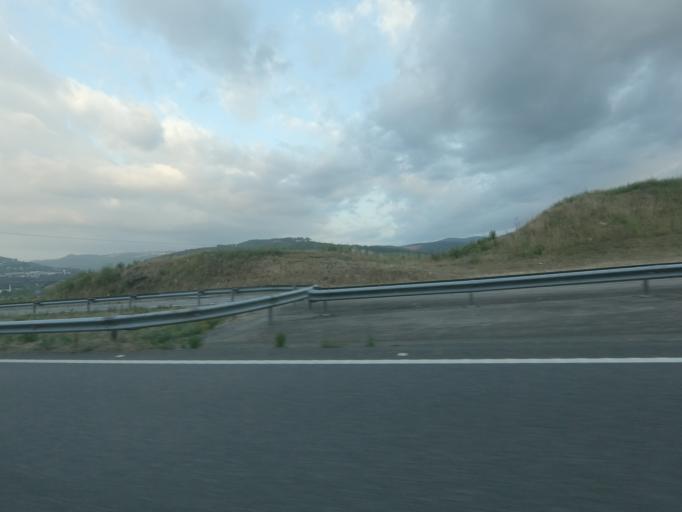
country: ES
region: Galicia
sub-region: Provincia de Ourense
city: Punxin
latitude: 42.3430
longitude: -8.0114
